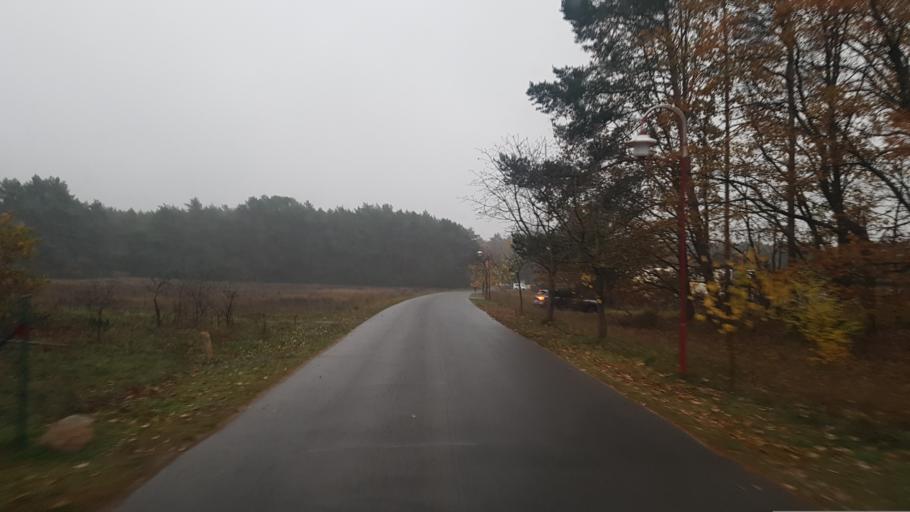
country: DE
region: Brandenburg
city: Beelitz
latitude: 52.2482
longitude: 12.9905
